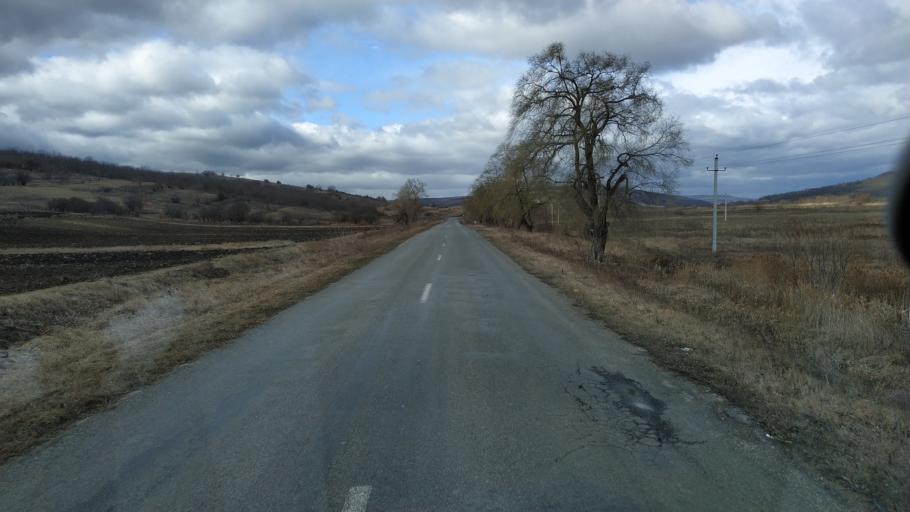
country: MD
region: Stinga Nistrului
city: Bucovat
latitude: 47.1425
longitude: 28.3731
